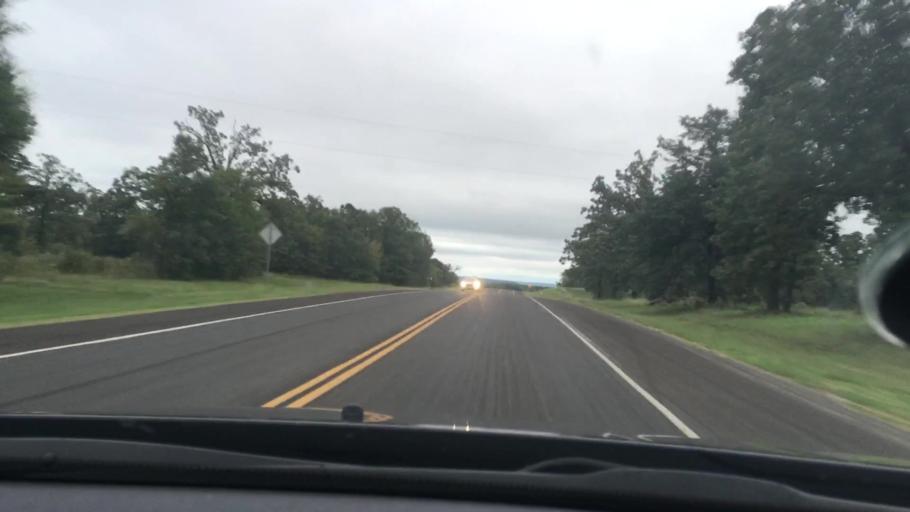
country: US
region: Oklahoma
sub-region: Sequoyah County
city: Vian
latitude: 35.5540
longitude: -94.9752
